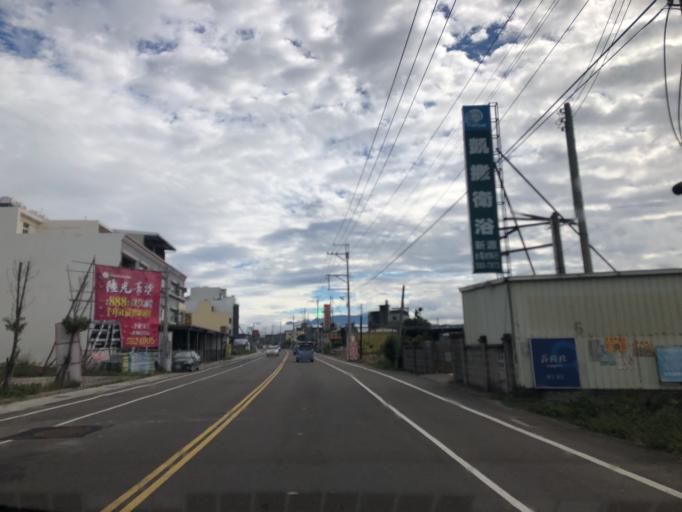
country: TW
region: Taiwan
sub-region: Hsinchu
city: Zhubei
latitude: 24.8262
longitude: 121.0705
